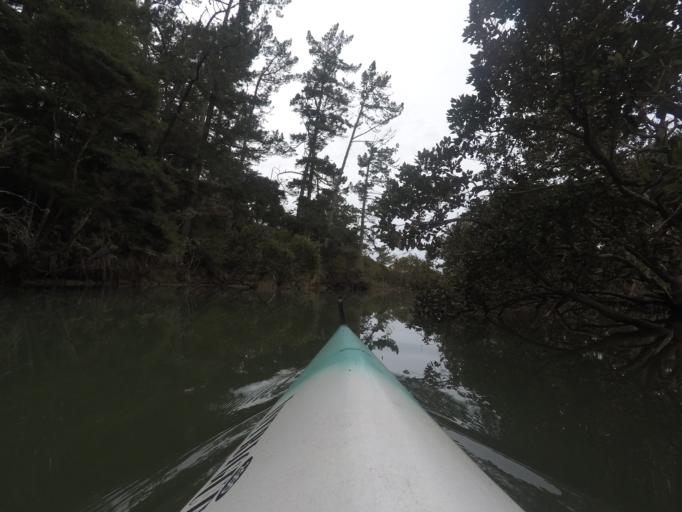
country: NZ
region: Auckland
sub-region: Auckland
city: Rothesay Bay
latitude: -36.6796
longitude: 174.7061
